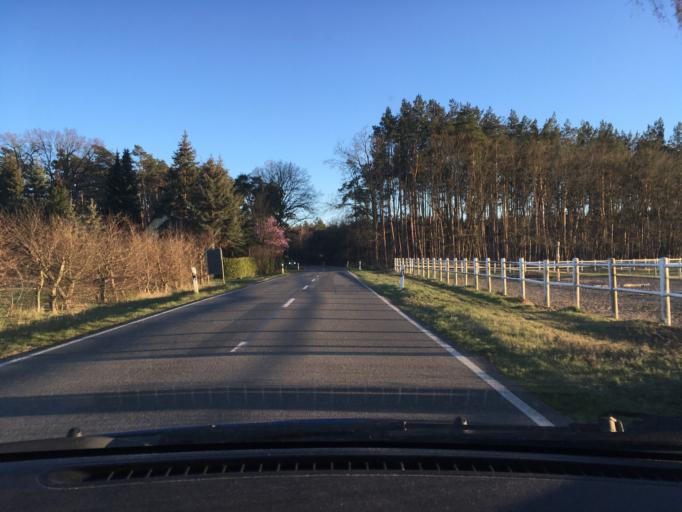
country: DE
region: Lower Saxony
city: Bleckede
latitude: 53.2590
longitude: 10.7428
